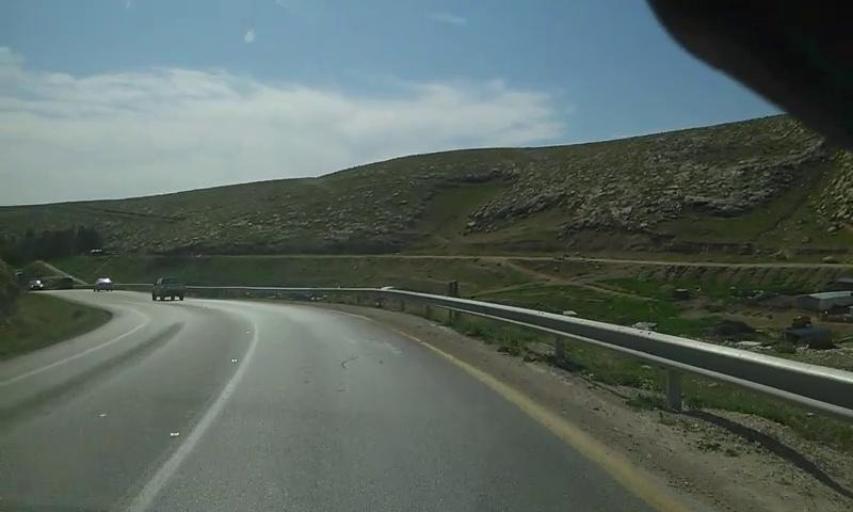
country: PS
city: Az Za`ayyim
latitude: 31.8067
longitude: 35.3087
